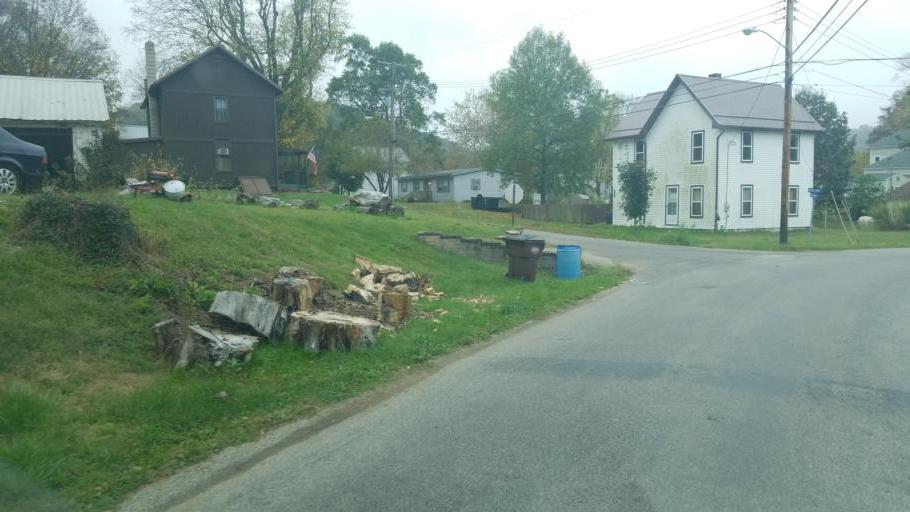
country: US
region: Ohio
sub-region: Ashland County
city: Loudonville
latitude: 40.5211
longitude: -82.0992
